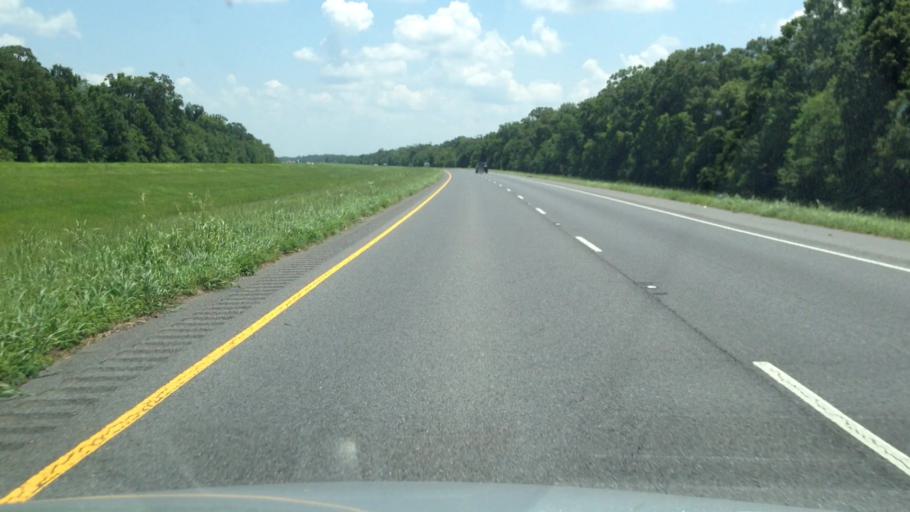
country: US
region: Louisiana
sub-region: Avoyelles Parish
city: Bunkie
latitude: 30.8366
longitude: -92.2288
